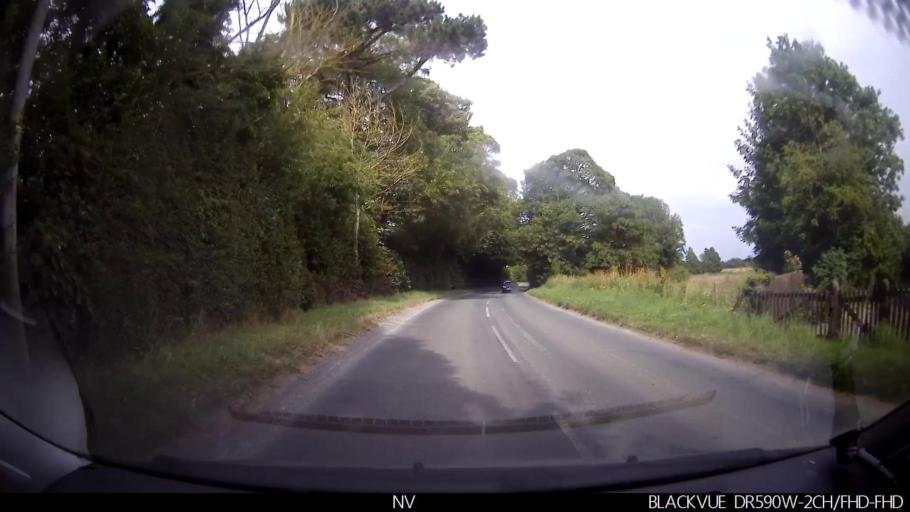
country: GB
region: England
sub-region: North Yorkshire
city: Great Habton
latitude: 54.2055
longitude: -0.8027
